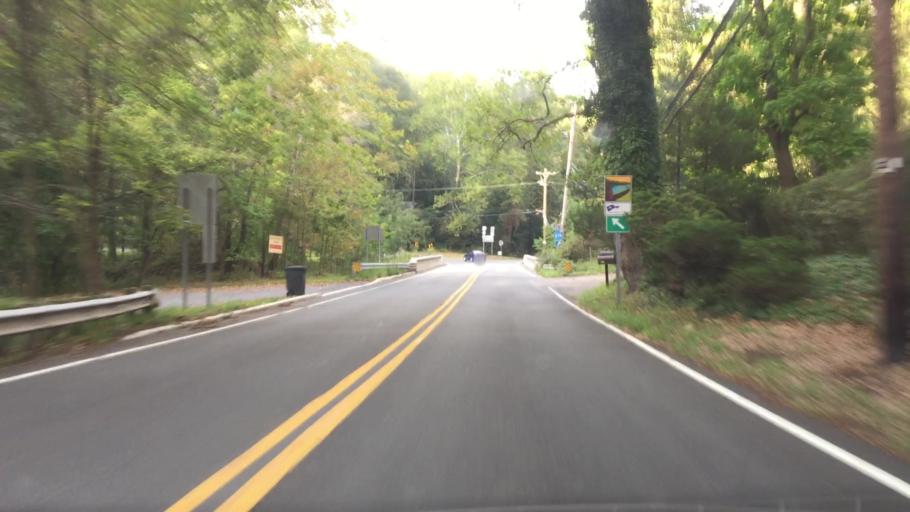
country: US
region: Pennsylvania
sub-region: Bucks County
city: New Hope
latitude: 40.4109
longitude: -74.9861
